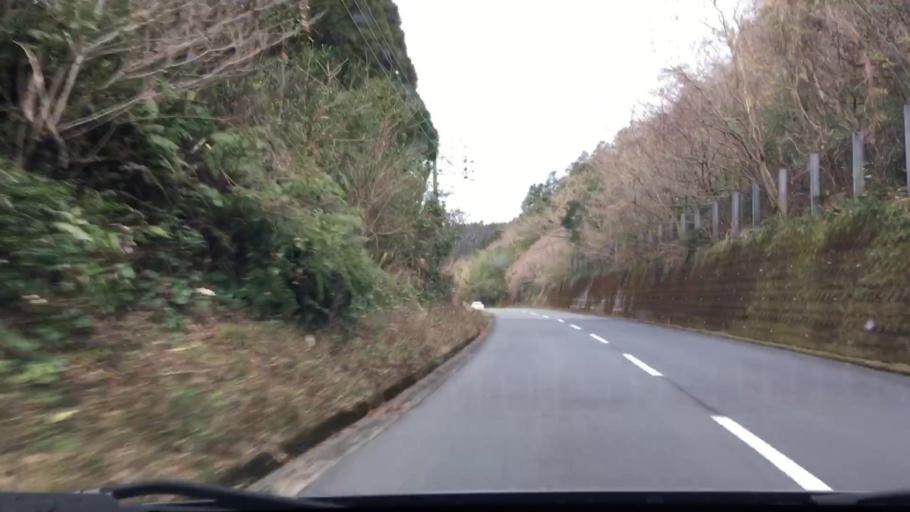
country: JP
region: Miyazaki
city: Nichinan
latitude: 31.6639
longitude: 131.3171
